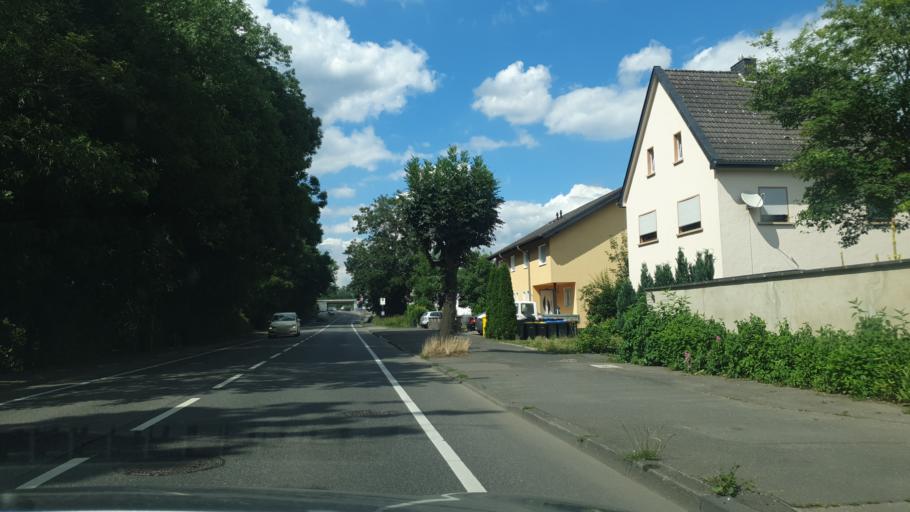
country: DE
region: Rheinland-Pfalz
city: Sinzig
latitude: 50.5521
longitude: 7.2443
